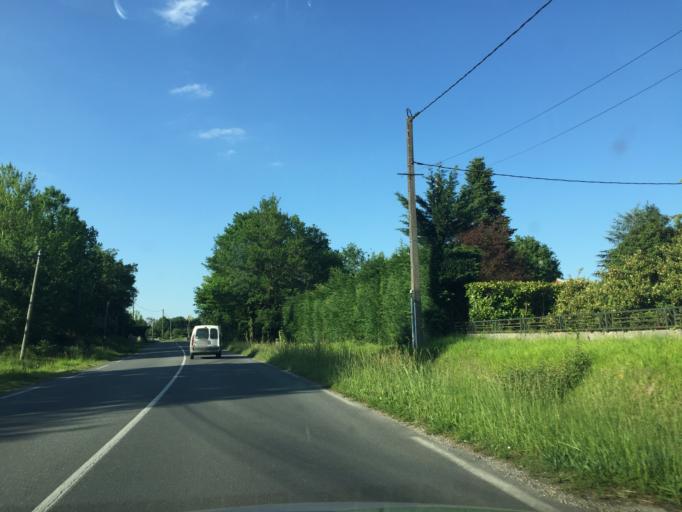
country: FR
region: Poitou-Charentes
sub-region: Departement de la Charente-Maritime
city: Saint-Aigulin
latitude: 45.1303
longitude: -0.0064
